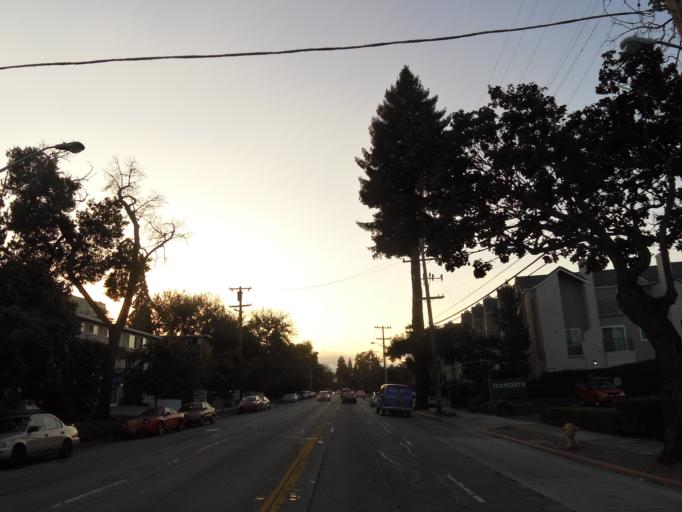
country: US
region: California
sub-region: San Mateo County
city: San Mateo
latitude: 37.5672
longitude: -122.3303
